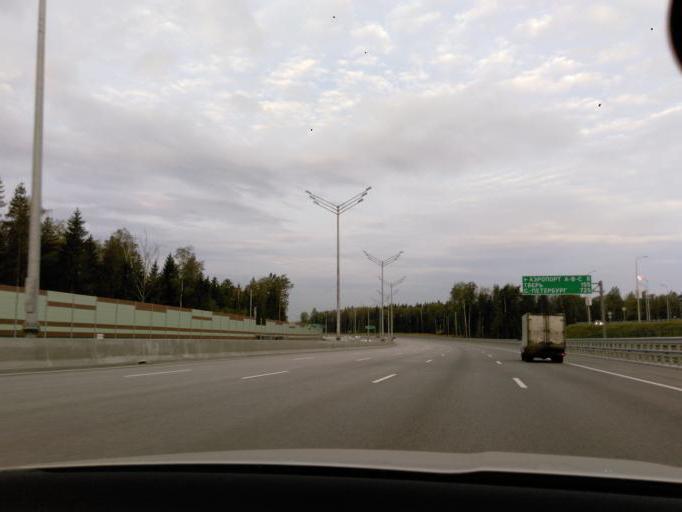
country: RU
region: Moskovskaya
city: Novopodrezkovo
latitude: 55.9593
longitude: 37.4040
